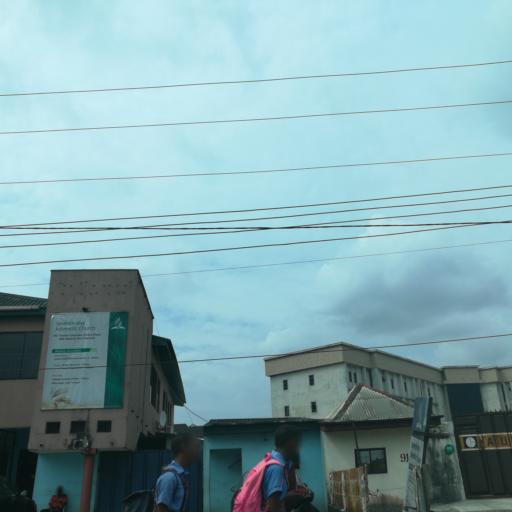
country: NG
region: Rivers
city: Port Harcourt
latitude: 4.8248
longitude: 6.9895
